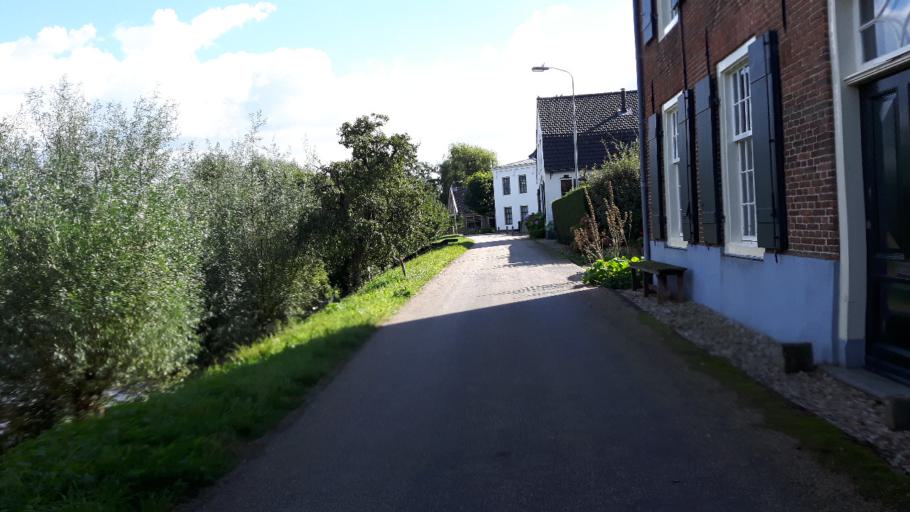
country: NL
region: South Holland
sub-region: Gemeente Leerdam
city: Leerdam
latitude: 51.8796
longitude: 5.1366
